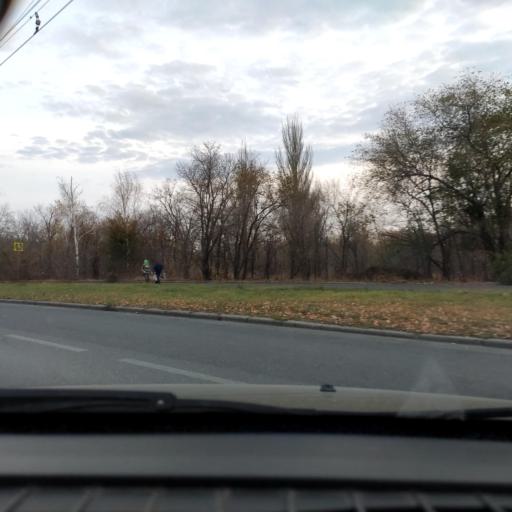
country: RU
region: Samara
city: Tol'yatti
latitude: 53.5003
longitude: 49.2670
